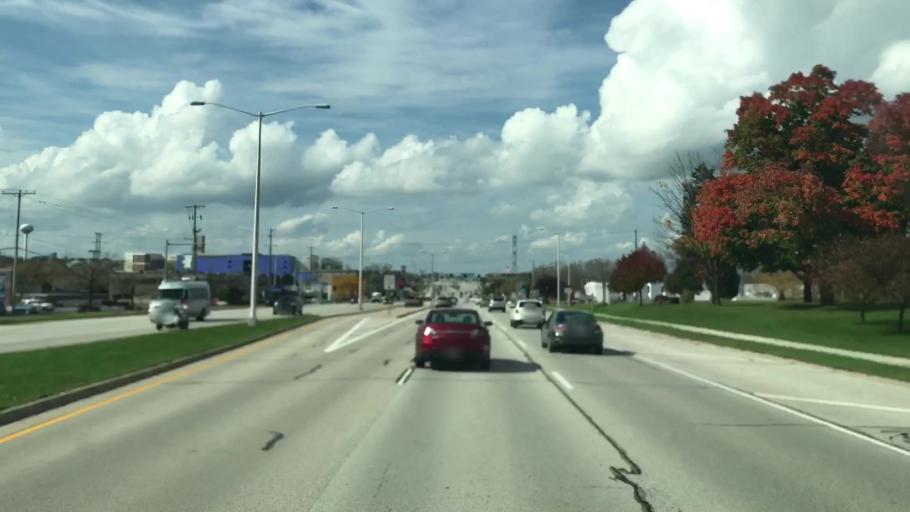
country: US
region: Wisconsin
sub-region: Waukesha County
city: Brookfield
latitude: 43.0362
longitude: -88.1546
